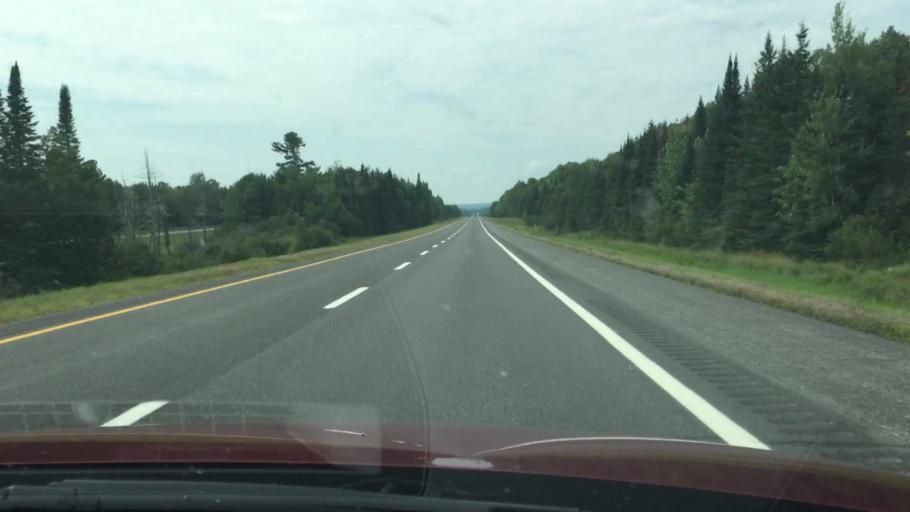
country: US
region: Maine
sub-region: Aroostook County
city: Houlton
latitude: 46.1414
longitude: -67.9617
